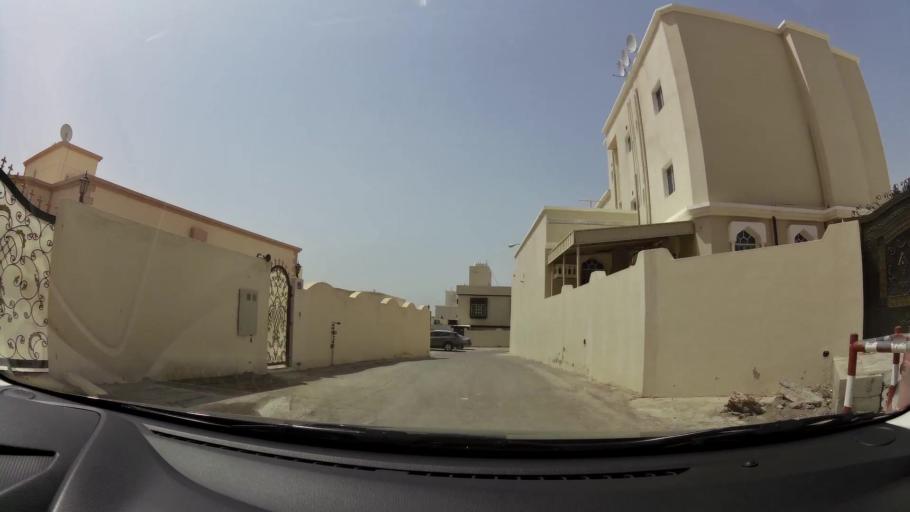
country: OM
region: Muhafazat Masqat
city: Bawshar
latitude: 23.5328
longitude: 58.3842
